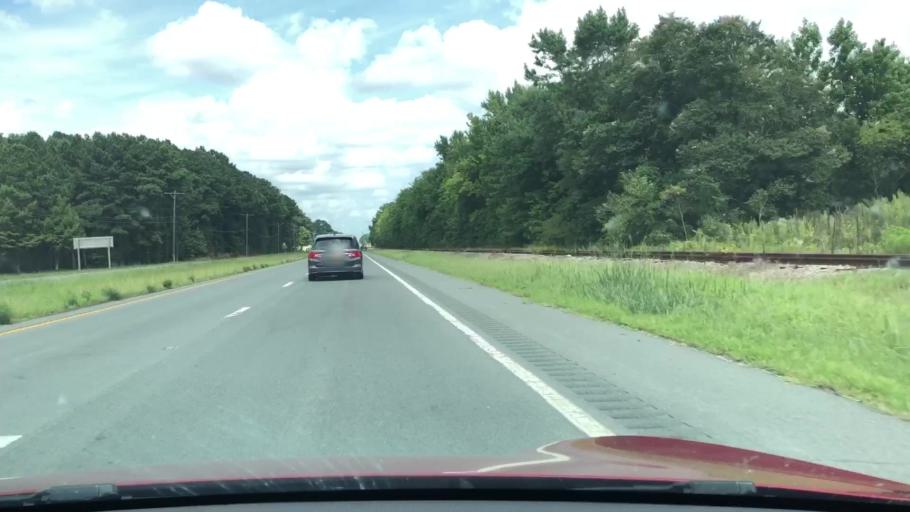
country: US
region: Virginia
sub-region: Accomack County
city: Onancock
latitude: 37.6399
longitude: -75.7490
